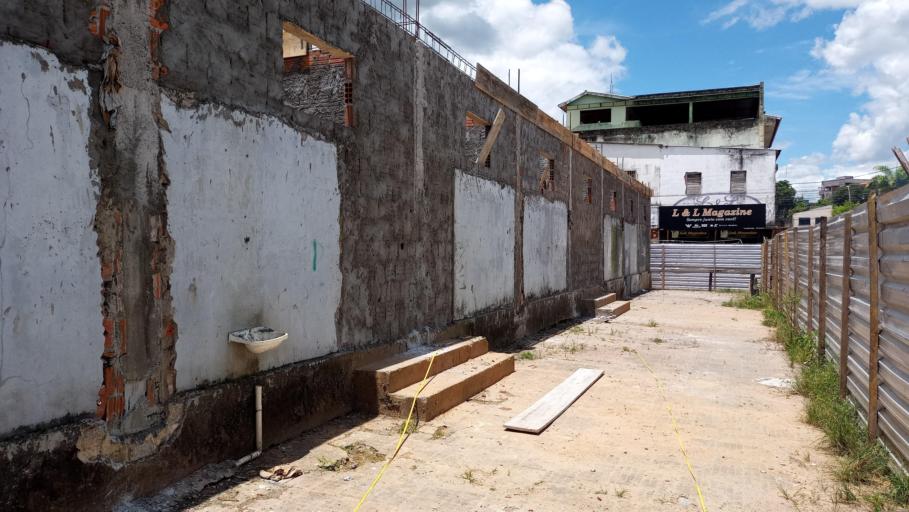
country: BR
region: Bahia
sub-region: Ubata
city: Ubata
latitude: -14.2173
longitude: -39.5180
